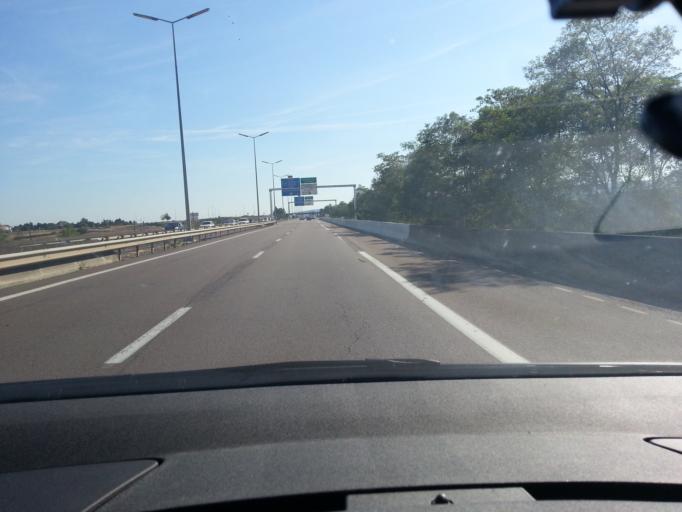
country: FR
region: Bourgogne
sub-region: Departement de la Cote-d'Or
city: Longvic
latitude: 47.2784
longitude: 5.0456
